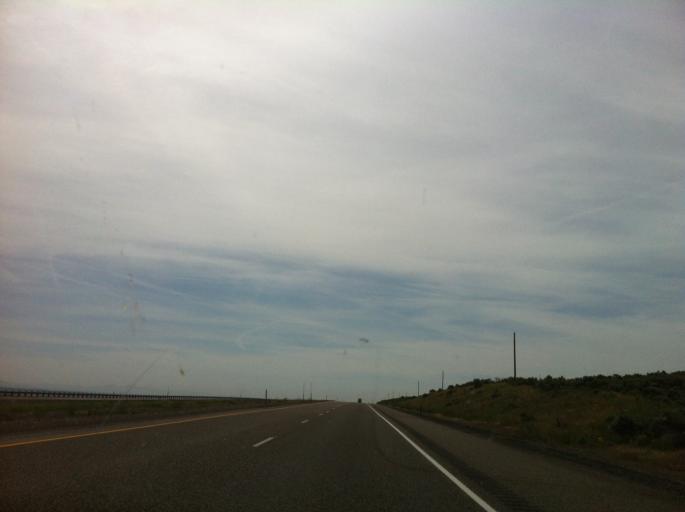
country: US
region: Oregon
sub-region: Malheur County
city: Ontario
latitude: 44.1175
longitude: -117.0647
